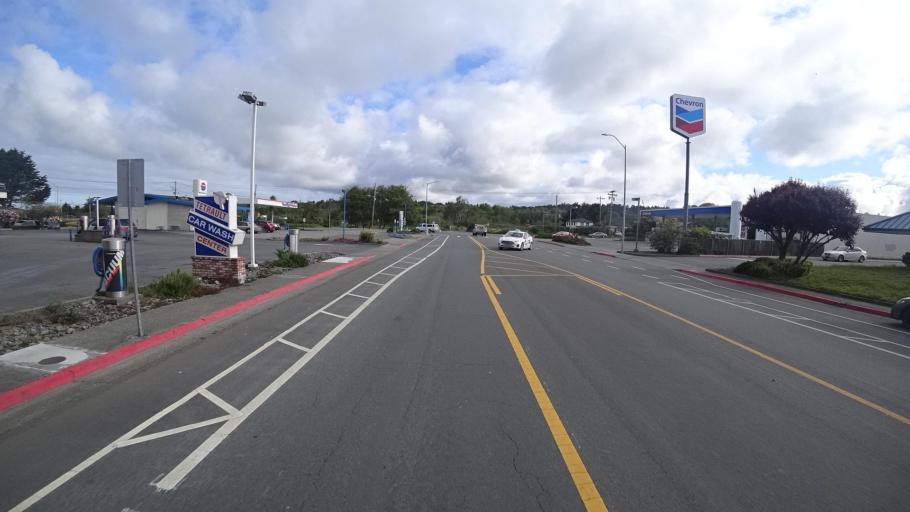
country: US
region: California
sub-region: Humboldt County
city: Arcata
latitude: 40.9043
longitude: -124.0831
